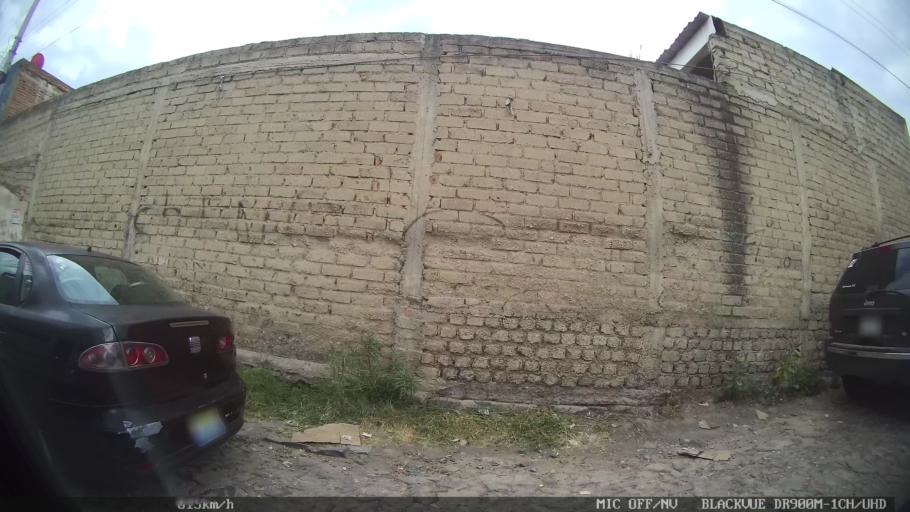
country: MX
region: Jalisco
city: Tlaquepaque
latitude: 20.6226
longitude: -103.2716
